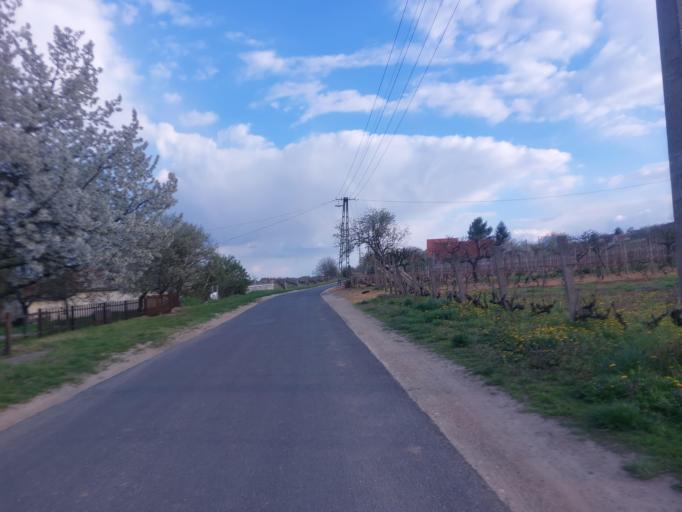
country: HU
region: Veszprem
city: Devecser
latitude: 47.1508
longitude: 17.3843
